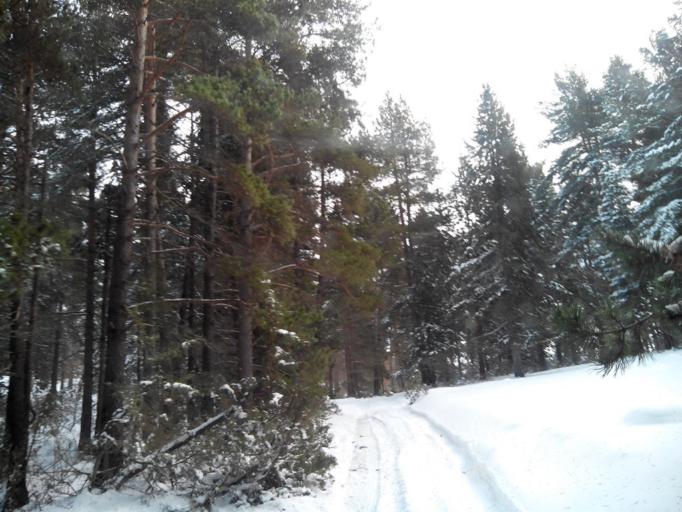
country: ES
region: Catalonia
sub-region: Provincia de Barcelona
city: Sant Julia de Cerdanyola
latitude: 42.2028
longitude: 1.9337
